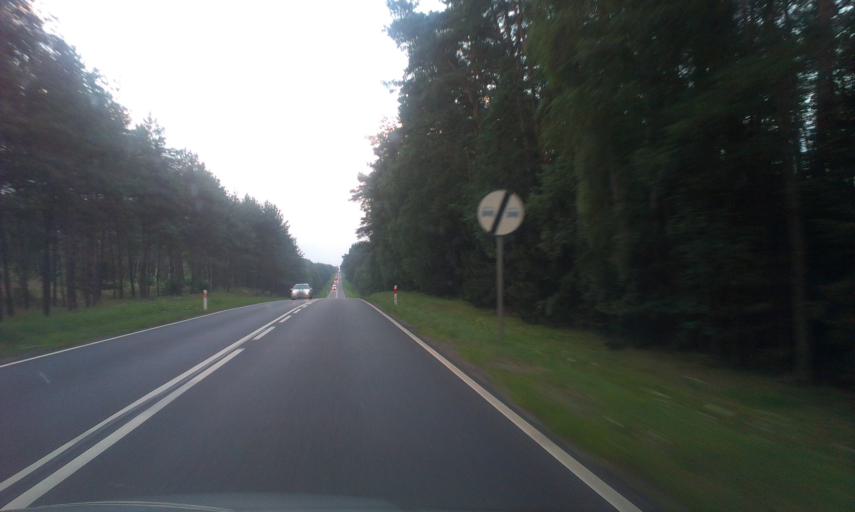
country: PL
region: West Pomeranian Voivodeship
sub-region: Powiat koszalinski
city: Sianow
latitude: 54.1099
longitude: 16.3315
